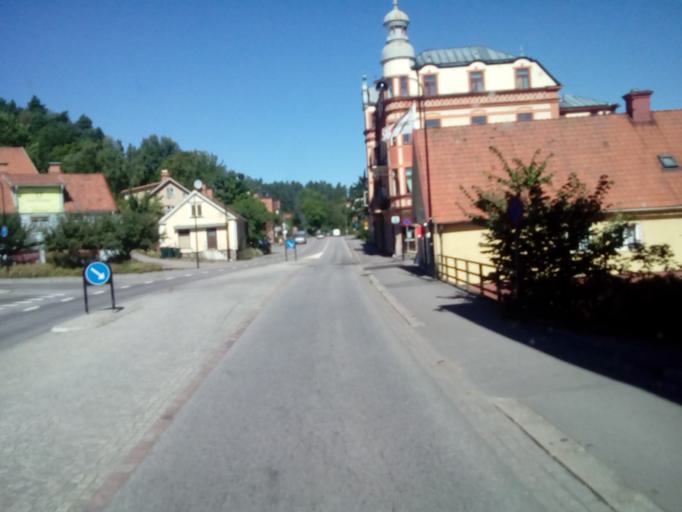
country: SE
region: OEstergoetland
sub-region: Kinda Kommun
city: Kisa
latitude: 57.9889
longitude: 15.6342
